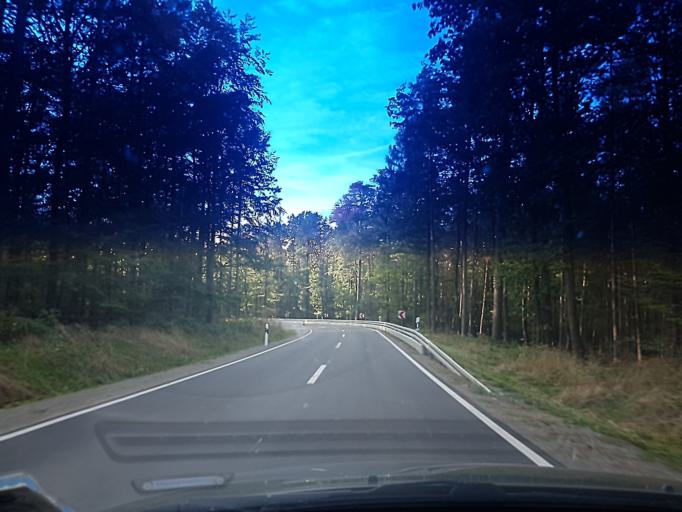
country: DE
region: Bavaria
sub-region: Regierungsbezirk Mittelfranken
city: Wachenroth
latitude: 49.7340
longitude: 10.6894
